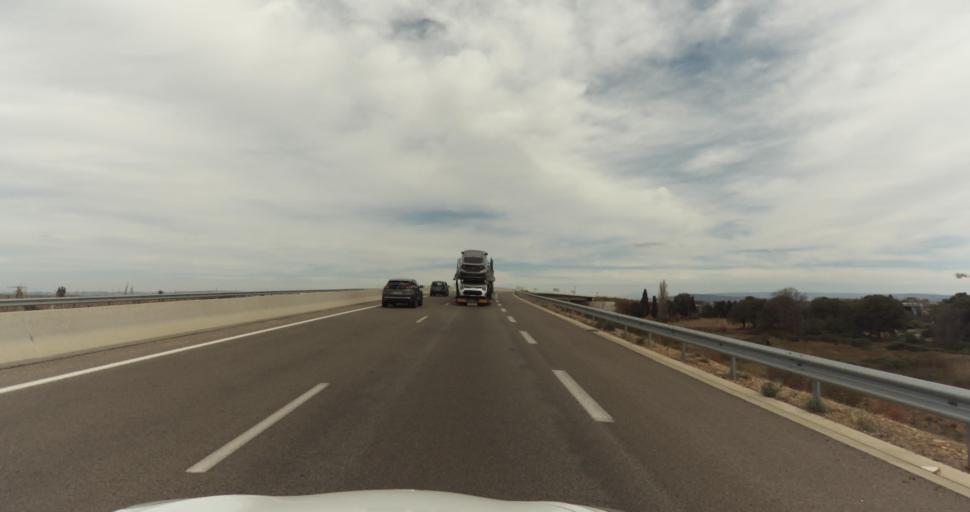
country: FR
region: Provence-Alpes-Cote d'Azur
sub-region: Departement des Bouches-du-Rhone
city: Miramas
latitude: 43.5942
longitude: 4.9893
